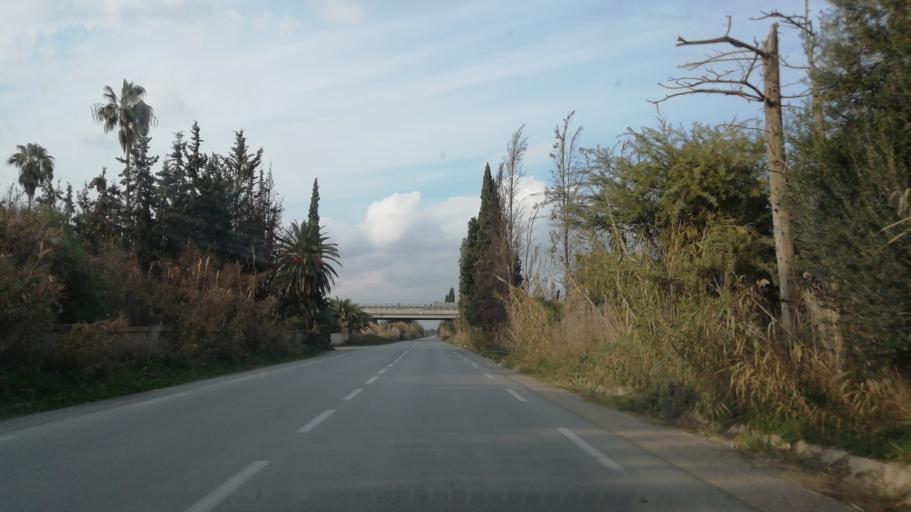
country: DZ
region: Mascara
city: Mascara
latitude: 35.6195
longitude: 0.0471
